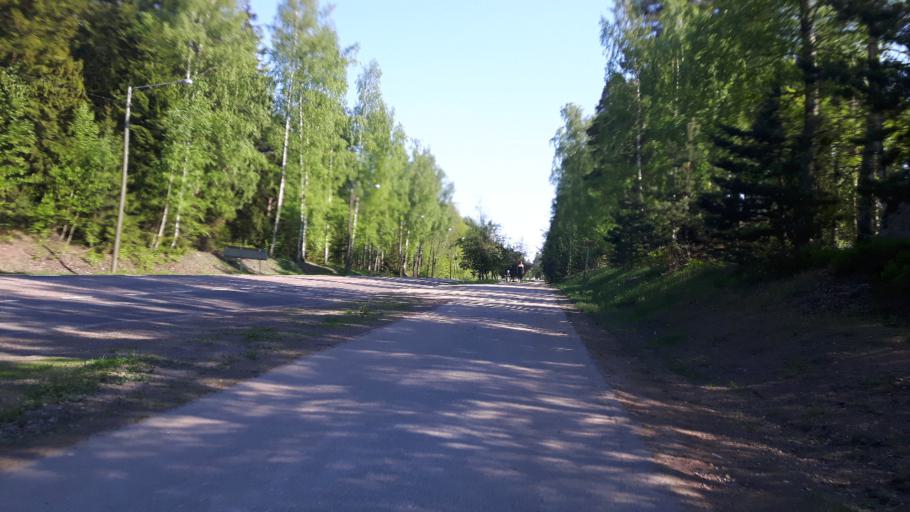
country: FI
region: Kymenlaakso
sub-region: Kotka-Hamina
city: Kotka
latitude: 60.4609
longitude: 26.8851
